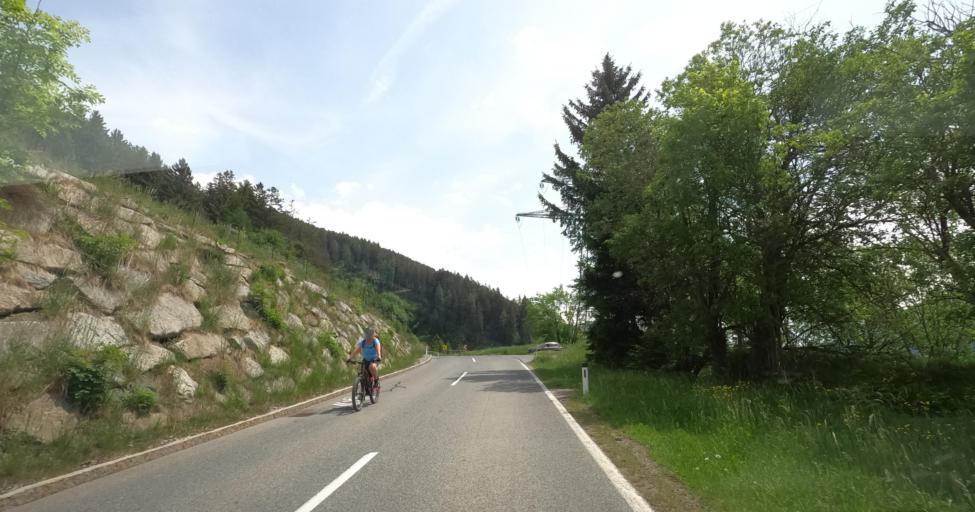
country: AT
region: Tyrol
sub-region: Politischer Bezirk Innsbruck Land
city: Patsch
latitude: 47.1992
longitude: 11.4211
